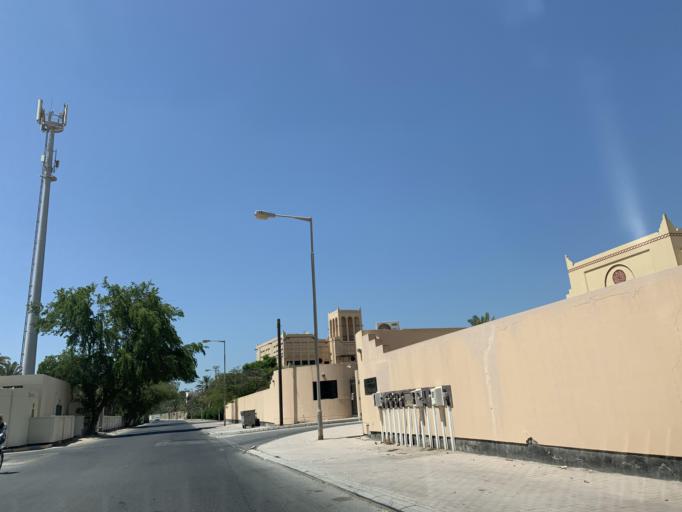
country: BH
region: Manama
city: Jidd Hafs
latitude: 26.2217
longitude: 50.4902
